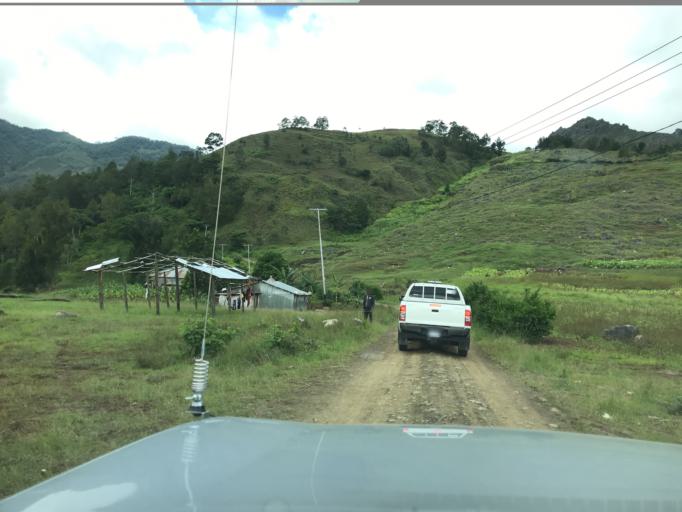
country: TL
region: Aileu
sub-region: Aileu Villa
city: Aileu
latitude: -8.8566
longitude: 125.5776
